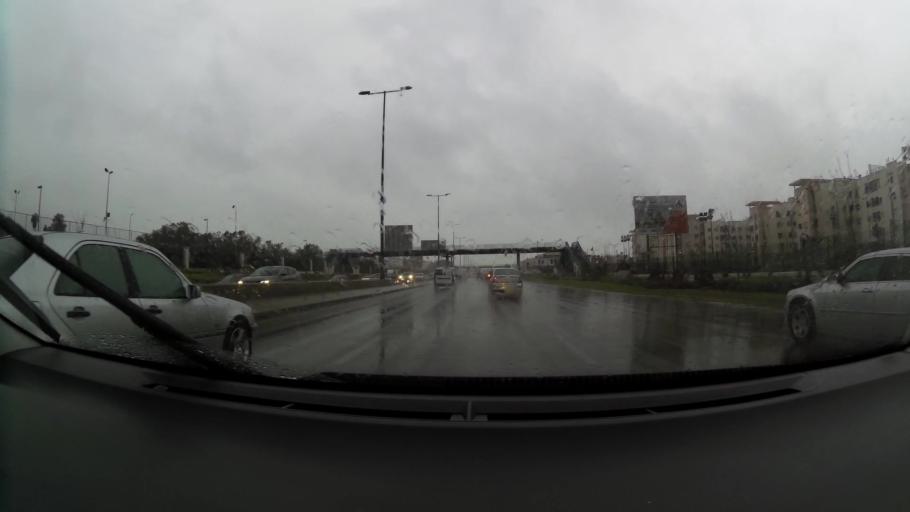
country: MA
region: Grand Casablanca
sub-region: Casablanca
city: Casablanca
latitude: 33.5652
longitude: -7.5796
